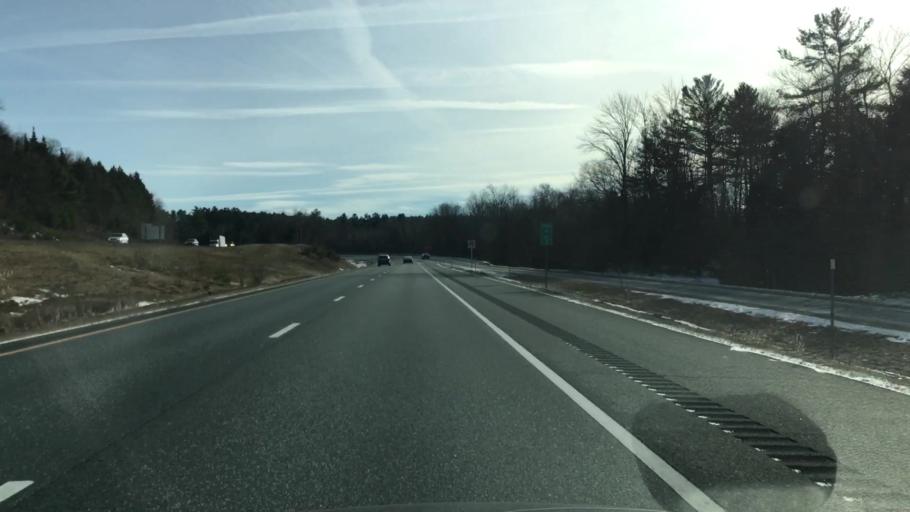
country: US
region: New Hampshire
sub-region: Sullivan County
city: Grantham
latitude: 43.4960
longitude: -72.1320
